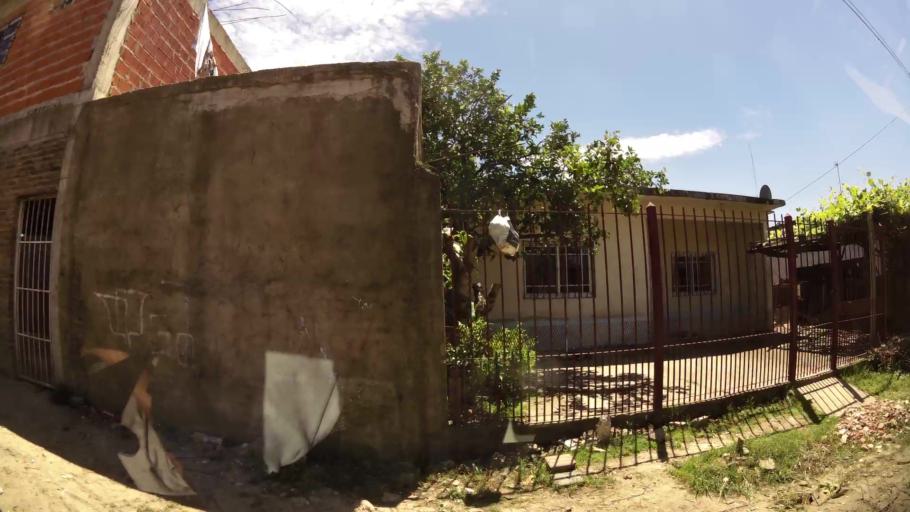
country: AR
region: Buenos Aires
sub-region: Partido de Lanus
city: Lanus
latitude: -34.7218
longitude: -58.3255
